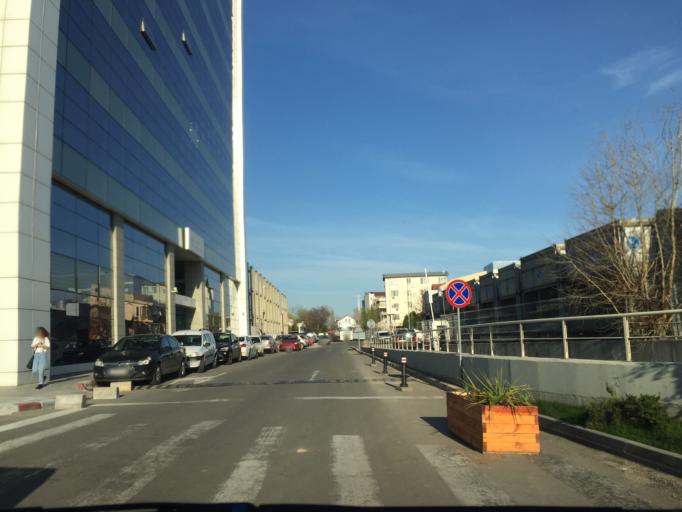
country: RO
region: Ilfov
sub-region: Comuna Chiajna
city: Rosu
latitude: 44.4295
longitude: 26.0354
